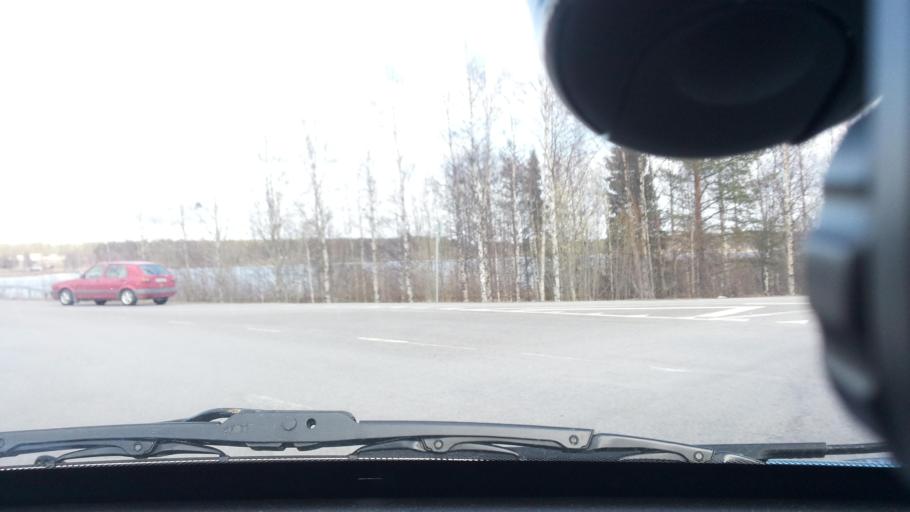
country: SE
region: Norrbotten
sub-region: Lulea Kommun
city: Gammelstad
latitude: 65.5867
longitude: 22.0279
